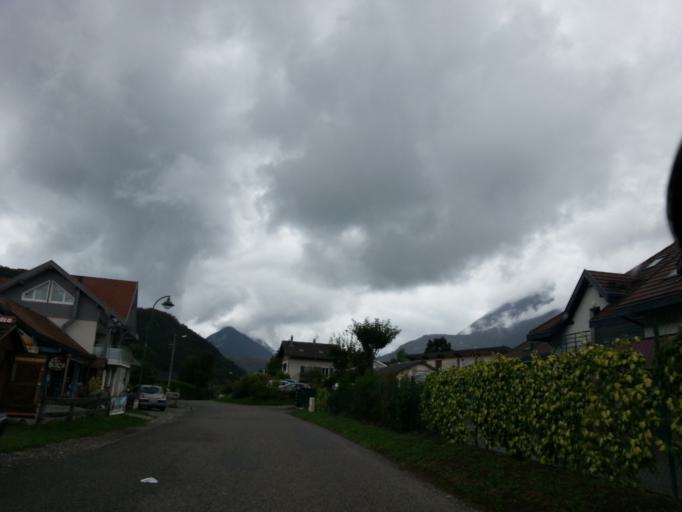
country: FR
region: Rhone-Alpes
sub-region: Departement de la Haute-Savoie
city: Talloires
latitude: 45.8099
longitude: 6.2095
